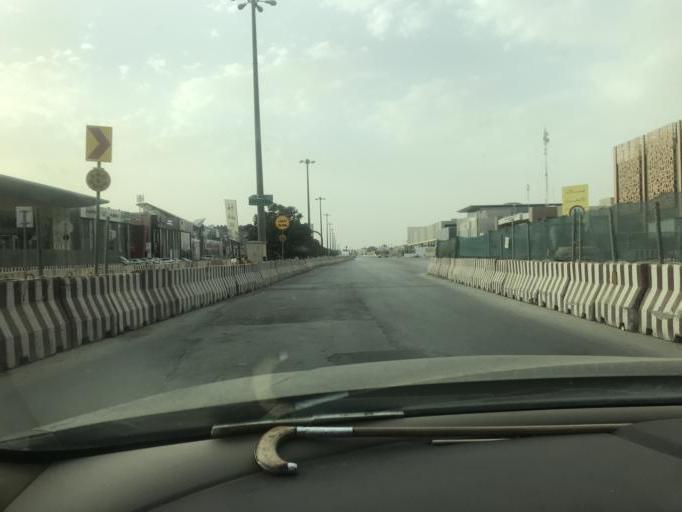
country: SA
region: Ar Riyad
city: Riyadh
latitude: 24.7868
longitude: 46.6599
